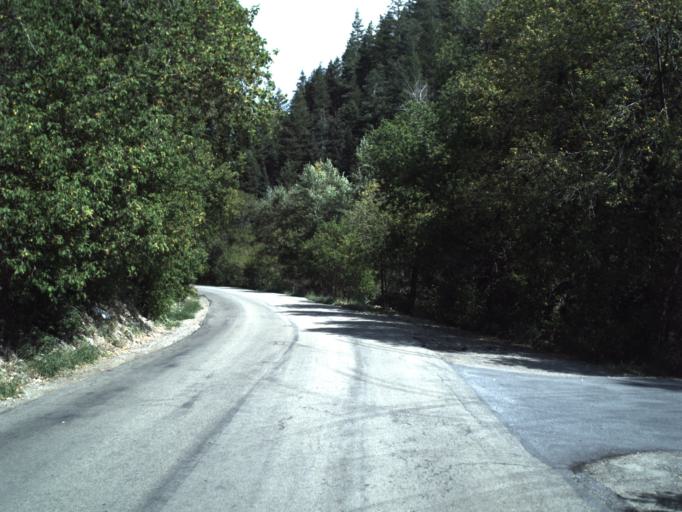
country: US
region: Utah
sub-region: Utah County
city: Highland
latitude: 40.4678
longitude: -111.6549
